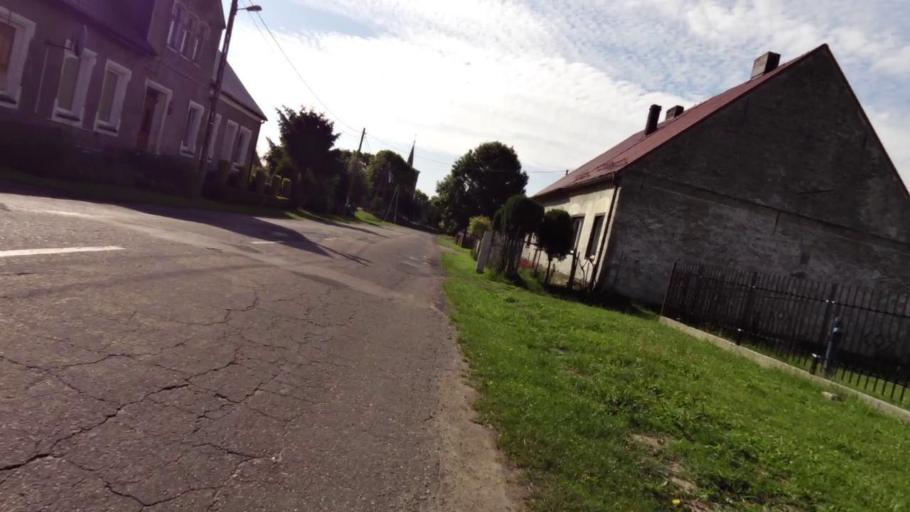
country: PL
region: West Pomeranian Voivodeship
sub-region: Powiat stargardzki
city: Marianowo
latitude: 53.3705
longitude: 15.3080
